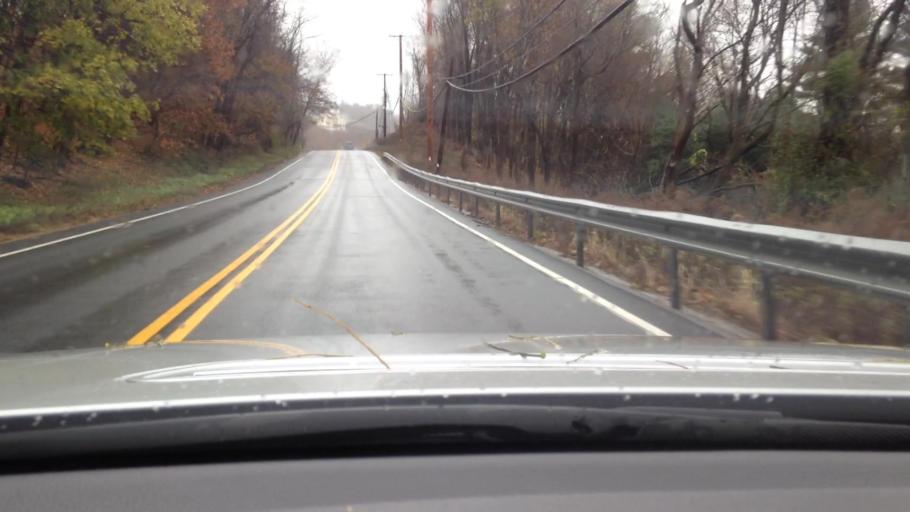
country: US
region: New York
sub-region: Putnam County
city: Cold Spring
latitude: 41.4074
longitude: -73.9334
